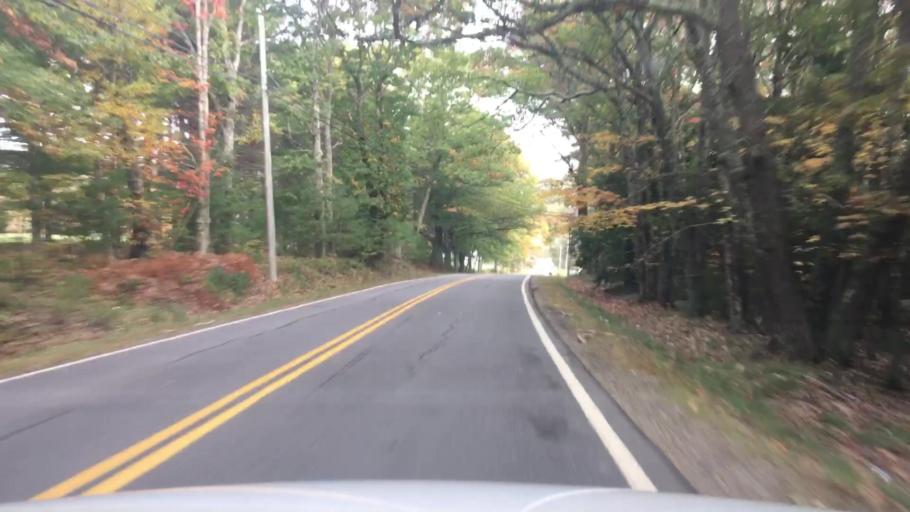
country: US
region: Maine
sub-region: Knox County
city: Hope
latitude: 44.2671
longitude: -69.1349
